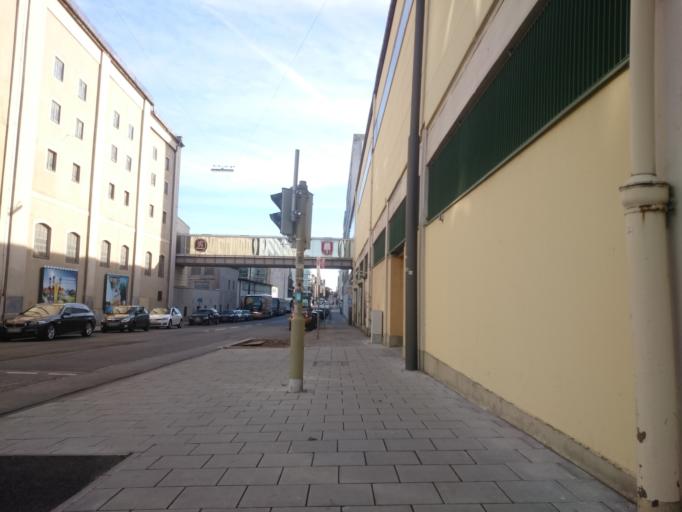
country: DE
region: Bavaria
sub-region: Upper Bavaria
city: Munich
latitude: 48.1465
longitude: 11.5546
